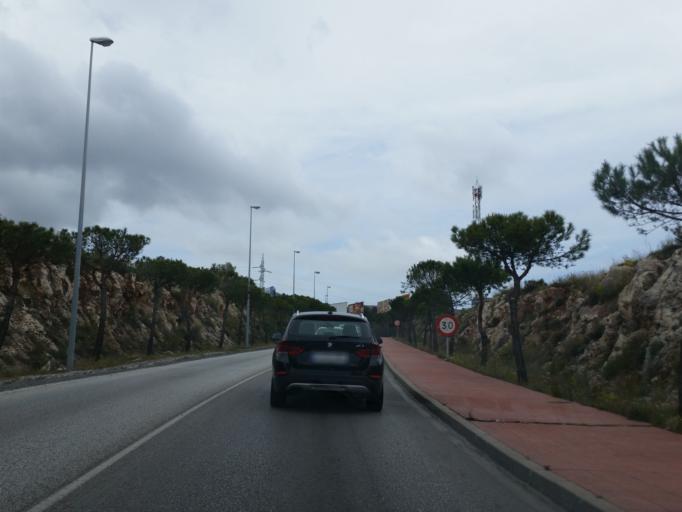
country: ES
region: Andalusia
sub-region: Provincia de Malaga
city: Benalmadena
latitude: 36.6081
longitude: -4.5346
